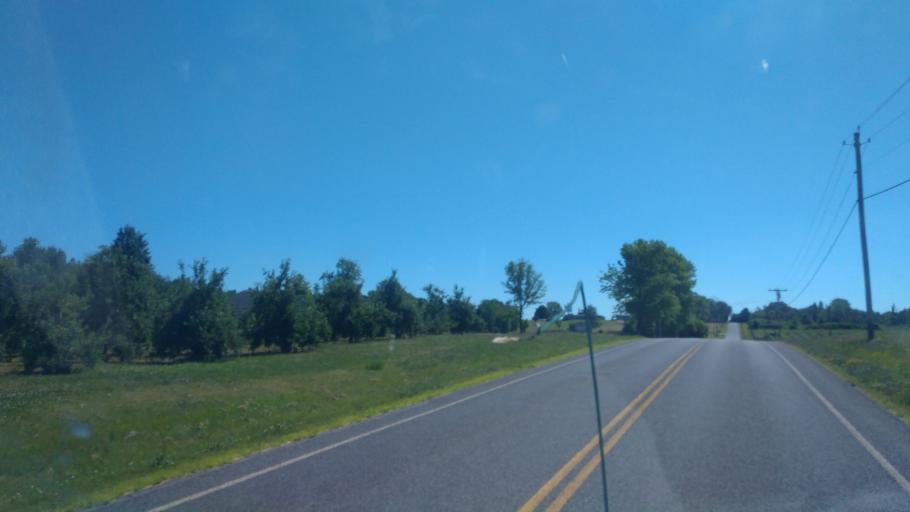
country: US
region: New York
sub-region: Wayne County
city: Sodus
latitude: 43.2732
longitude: -77.1055
